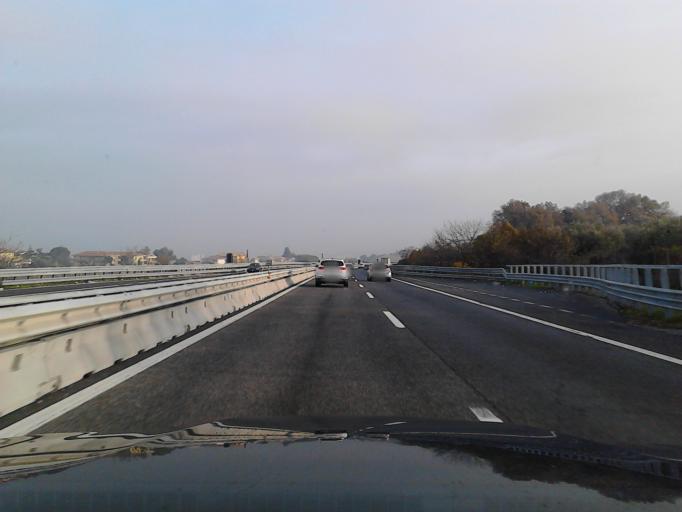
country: IT
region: Abruzzo
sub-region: Provincia di Teramo
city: Silvi
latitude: 42.5470
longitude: 14.1044
